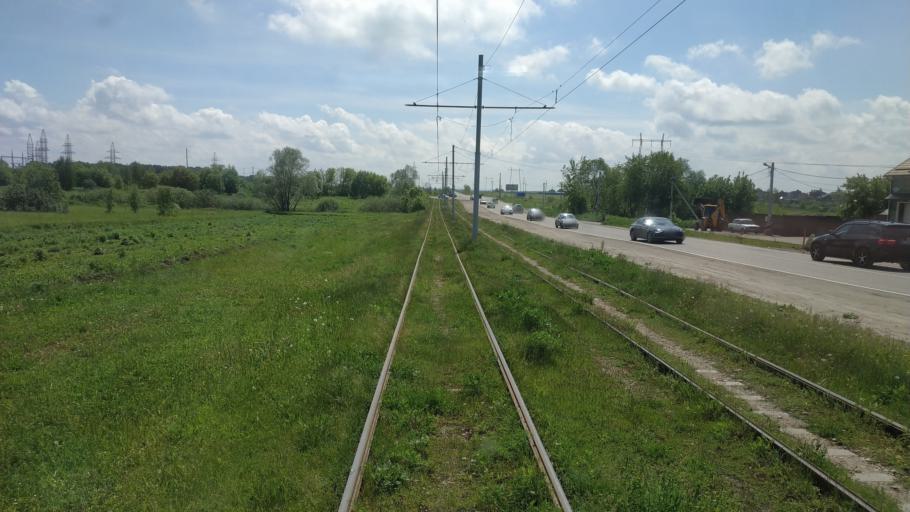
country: RU
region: Moskovskaya
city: Sychevo
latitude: 55.0616
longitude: 38.7263
